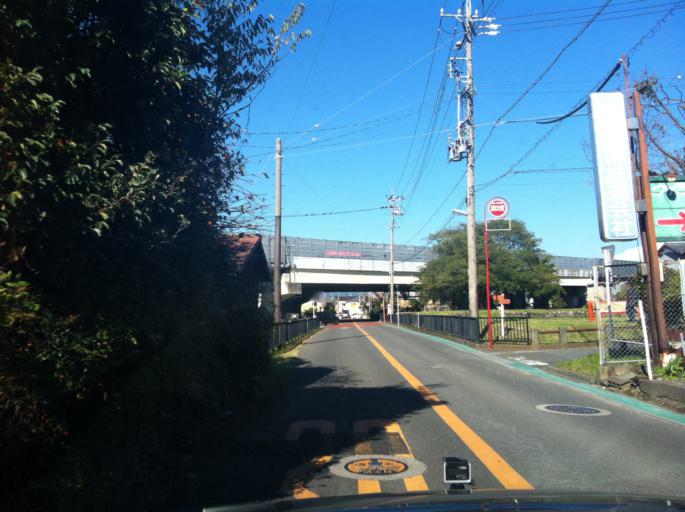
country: JP
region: Shizuoka
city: Shizuoka-shi
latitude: 34.9633
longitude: 138.4264
